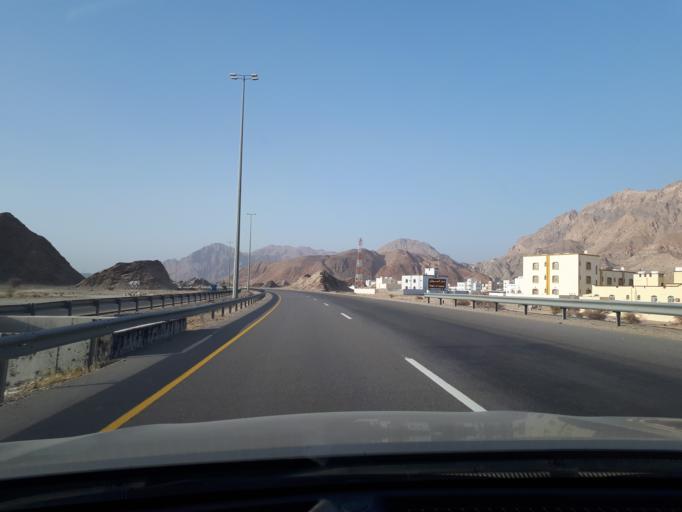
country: OM
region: Muhafazat Masqat
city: Bawshar
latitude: 23.4366
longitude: 58.5105
